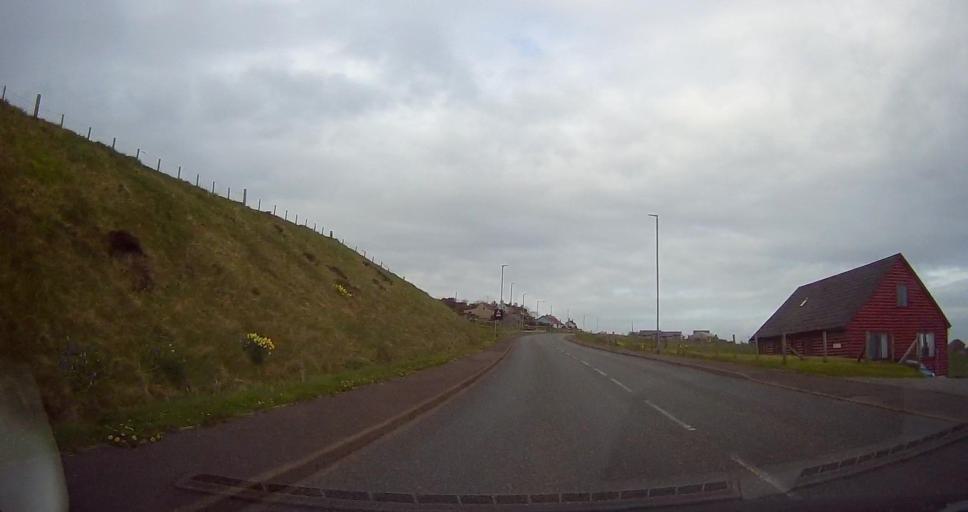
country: GB
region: Scotland
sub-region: Shetland Islands
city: Sandwick
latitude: 60.0423
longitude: -1.2292
